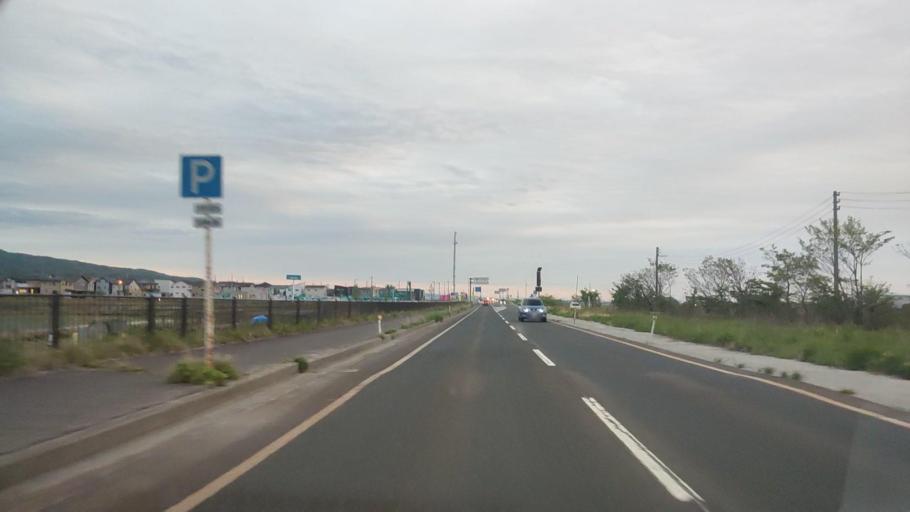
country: JP
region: Niigata
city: Niitsu-honcho
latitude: 37.7547
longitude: 139.0904
